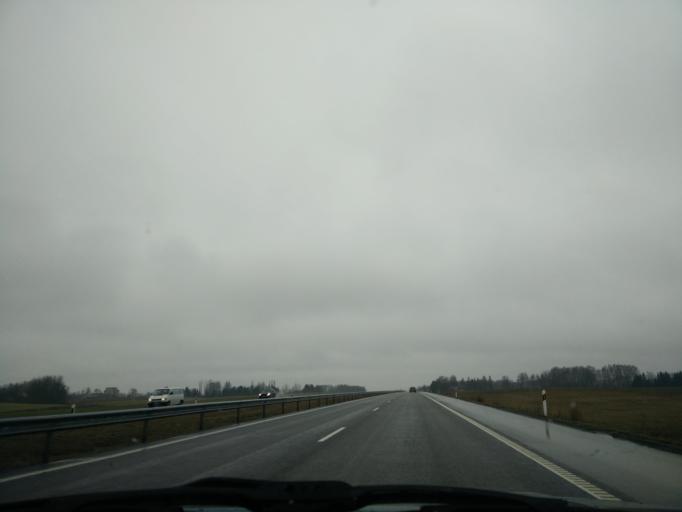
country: LT
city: Skaudvile
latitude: 55.4773
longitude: 22.6150
